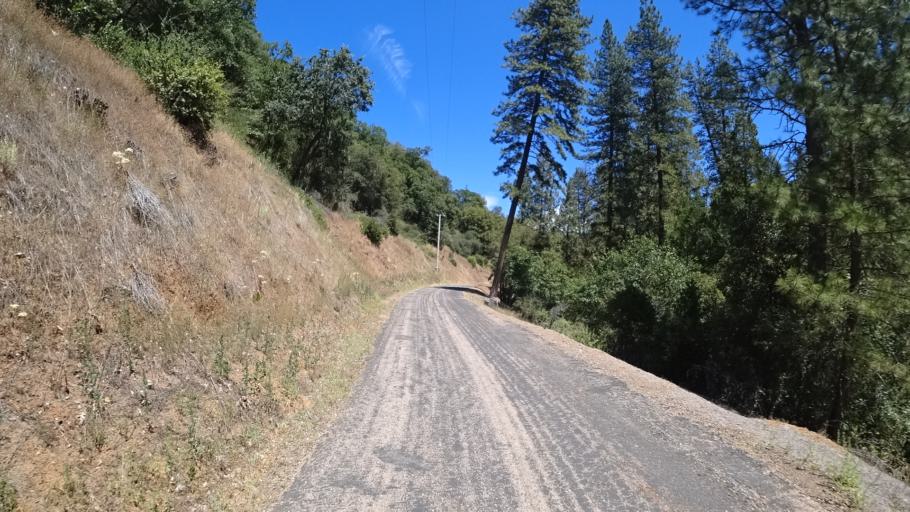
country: US
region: California
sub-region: Calaveras County
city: Forest Meadows
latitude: 38.2139
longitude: -120.4317
